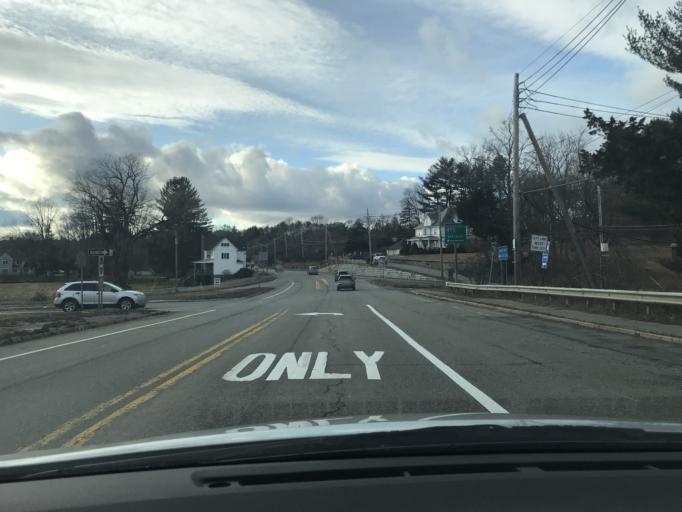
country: US
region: Massachusetts
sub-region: Middlesex County
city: Littleton Common
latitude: 42.5401
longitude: -71.4949
